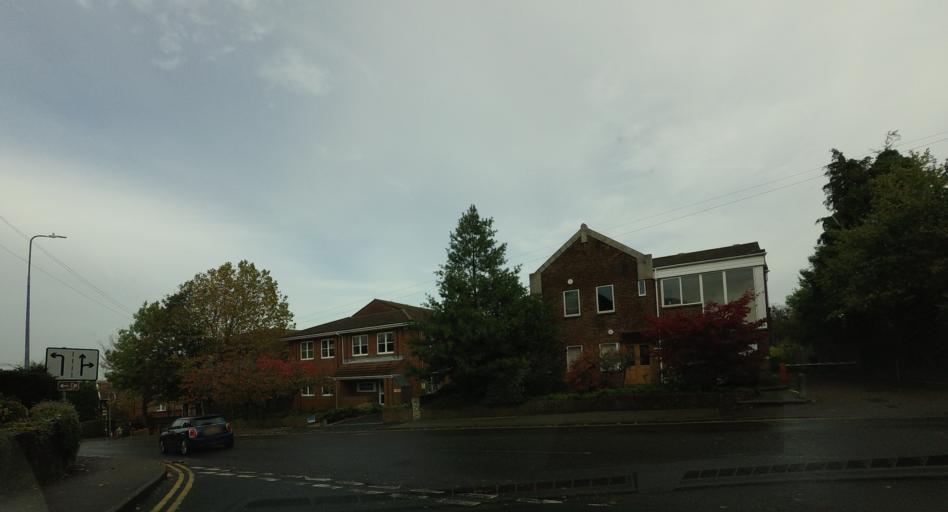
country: GB
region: England
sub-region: Kent
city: Sevenoaks
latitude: 51.2730
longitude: 0.1913
